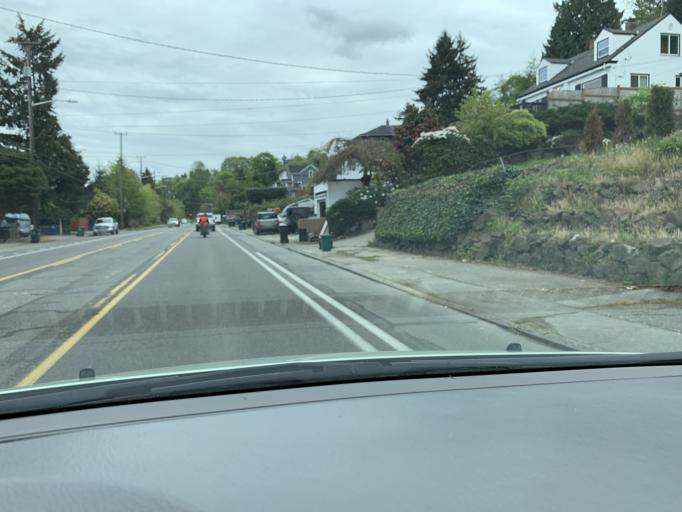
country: US
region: Washington
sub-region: King County
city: Bryn Mawr-Skyway
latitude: 47.5130
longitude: -122.2504
